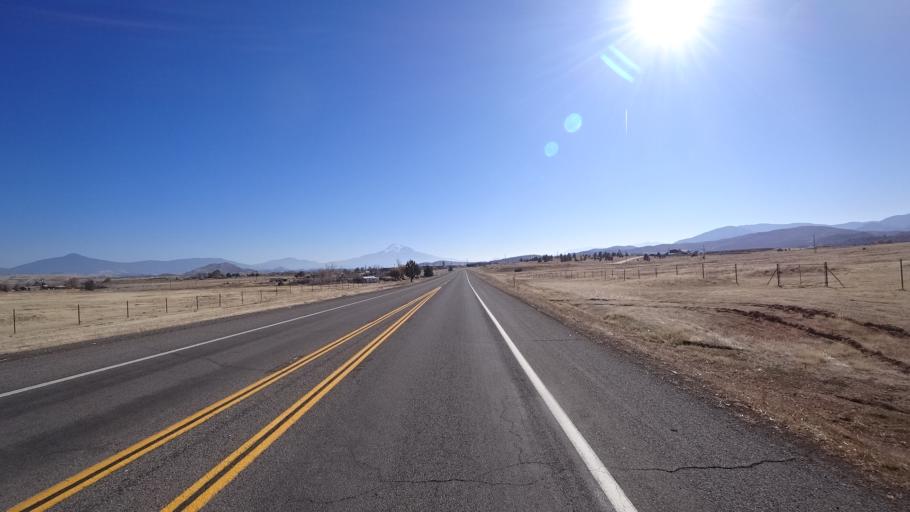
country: US
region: California
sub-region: Siskiyou County
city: Yreka
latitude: 41.7399
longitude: -122.5976
